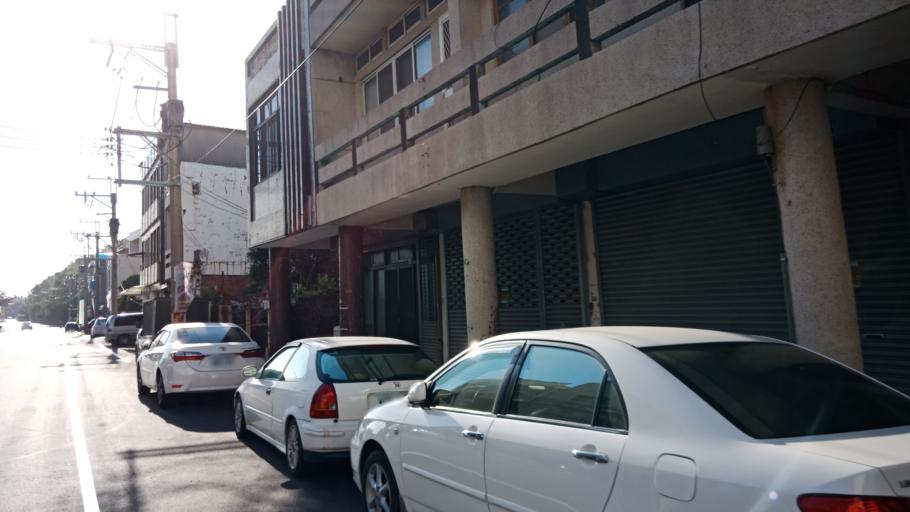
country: TW
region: Taiwan
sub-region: Miaoli
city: Miaoli
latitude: 24.4945
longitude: 120.6886
